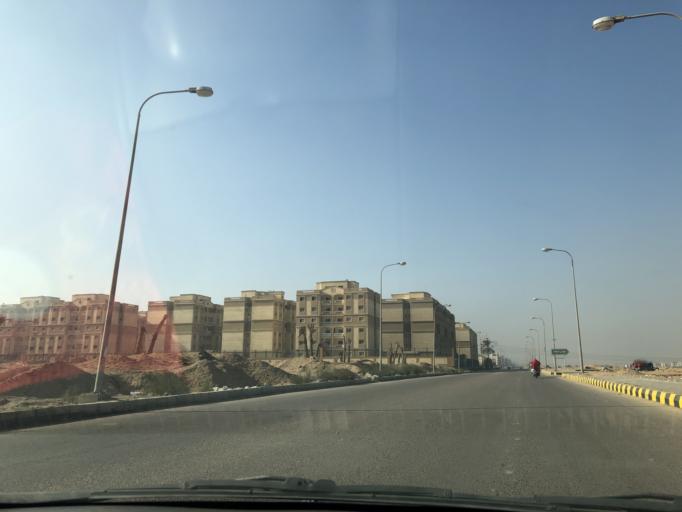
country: EG
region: Al Jizah
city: Madinat Sittah Uktubar
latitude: 29.9187
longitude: 31.0582
